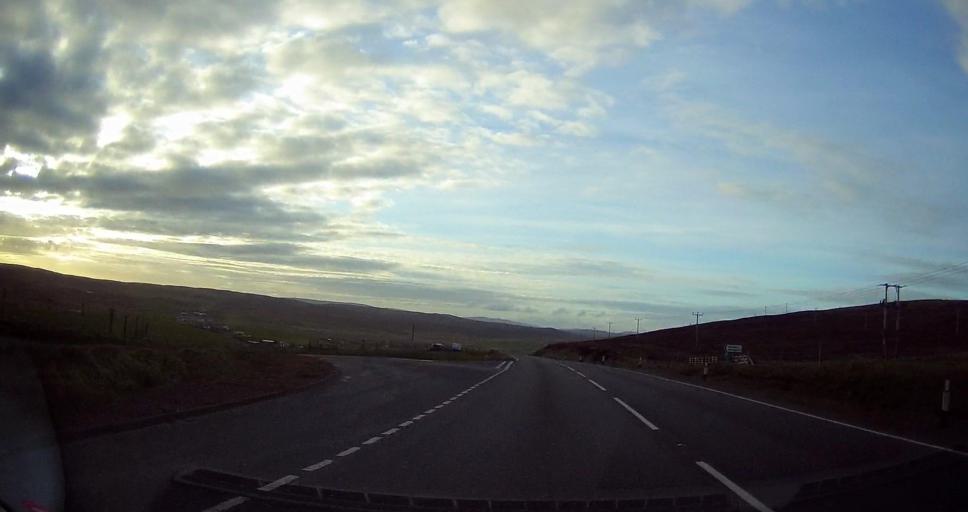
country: GB
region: Scotland
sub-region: Shetland Islands
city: Lerwick
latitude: 60.1763
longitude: -1.2231
